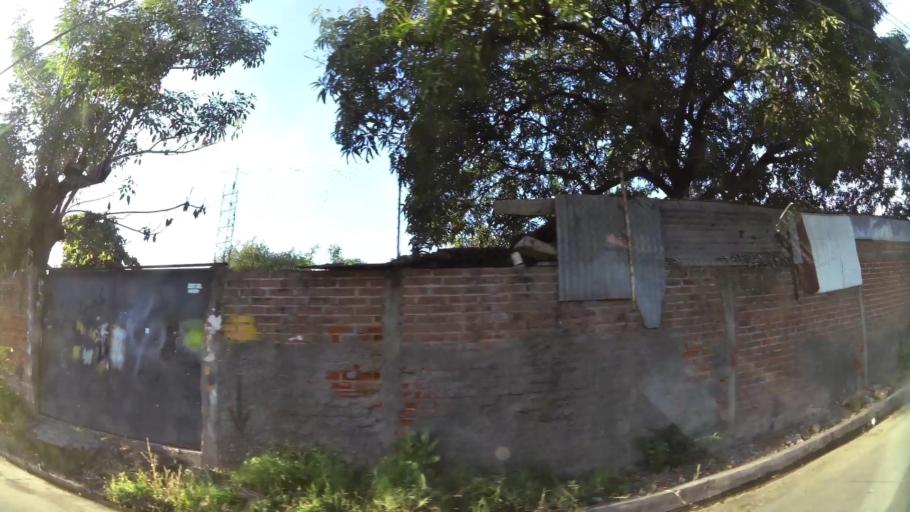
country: SV
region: San Miguel
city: San Miguel
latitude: 13.4682
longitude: -88.1676
